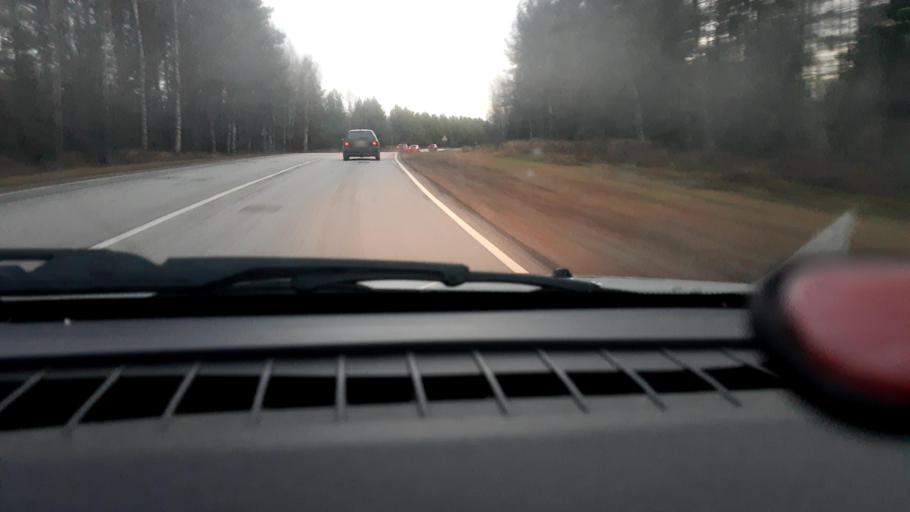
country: RU
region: Nizjnij Novgorod
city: Krasnyye Baki
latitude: 56.9874
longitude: 45.1178
